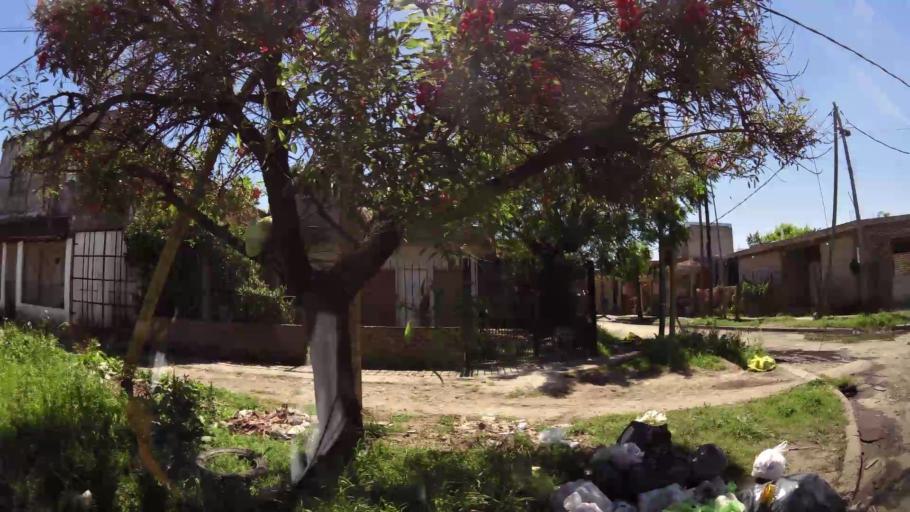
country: AR
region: Buenos Aires
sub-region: Partido de Lanus
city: Lanus
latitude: -34.7274
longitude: -58.3340
